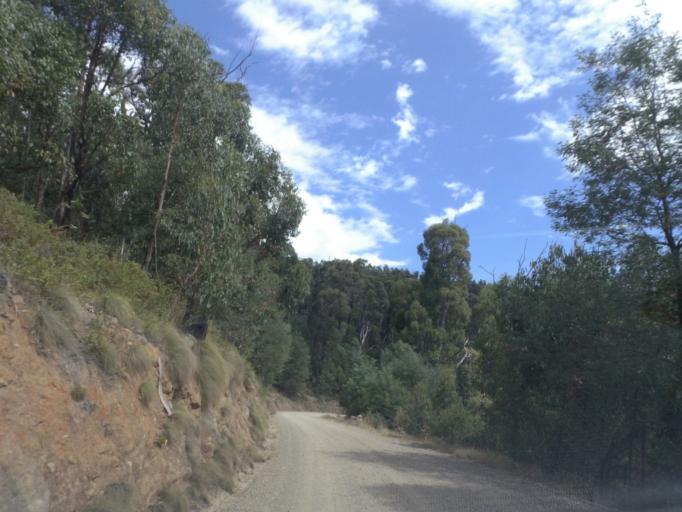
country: AU
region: Victoria
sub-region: Murrindindi
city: Alexandra
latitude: -37.4611
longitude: 145.7756
